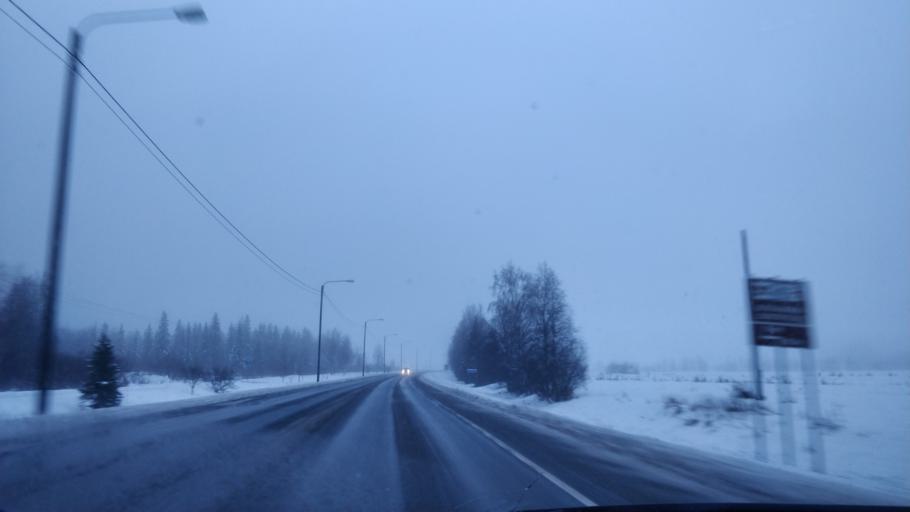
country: FI
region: Lapland
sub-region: Kemi-Tornio
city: Tervola
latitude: 66.1492
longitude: 24.9750
